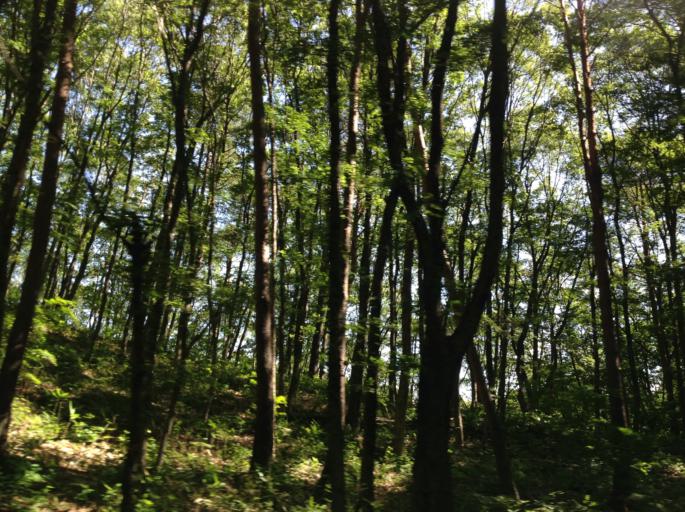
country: JP
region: Akita
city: Kakunodatemachi
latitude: 39.6975
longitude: 140.6636
